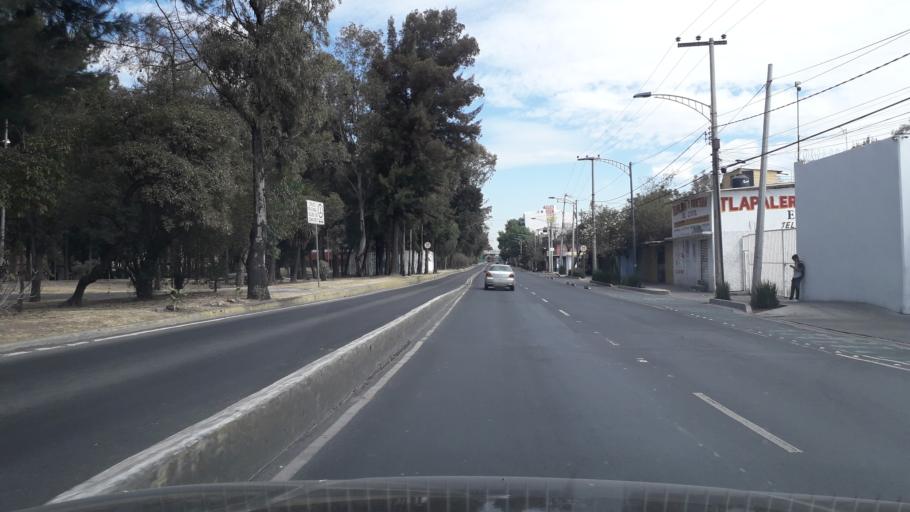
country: MX
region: Mexico City
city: Gustavo A. Madero
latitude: 19.4877
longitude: -99.0938
